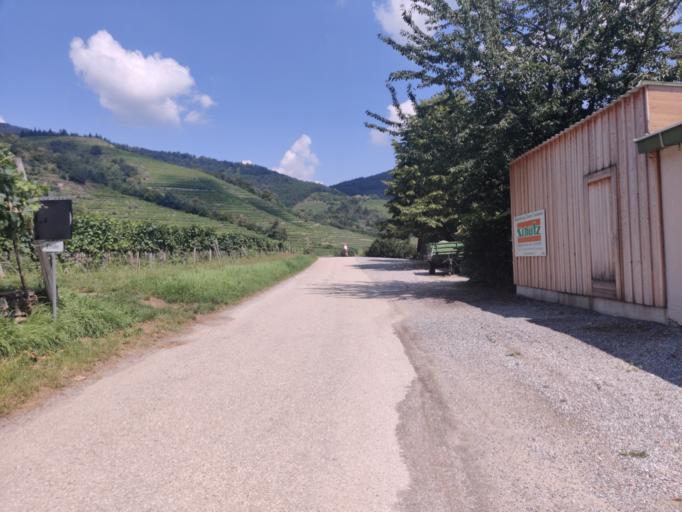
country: AT
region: Lower Austria
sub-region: Politischer Bezirk Krems
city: Durnstein
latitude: 48.4083
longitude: 15.4868
